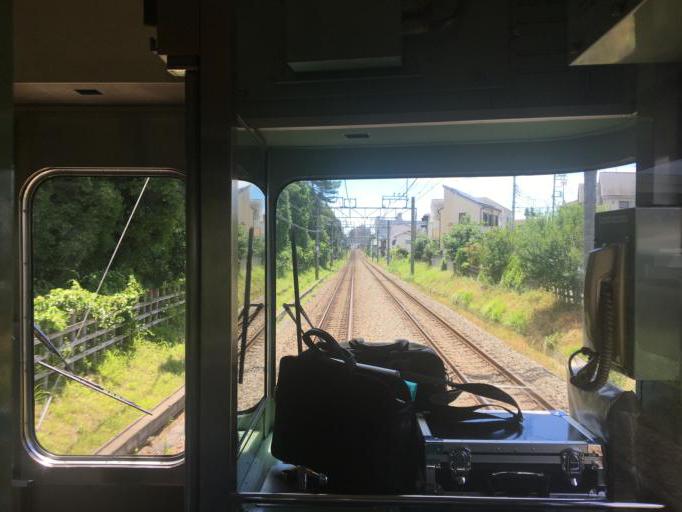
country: JP
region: Tokyo
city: Higashimurayama-shi
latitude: 35.7423
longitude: 139.4814
